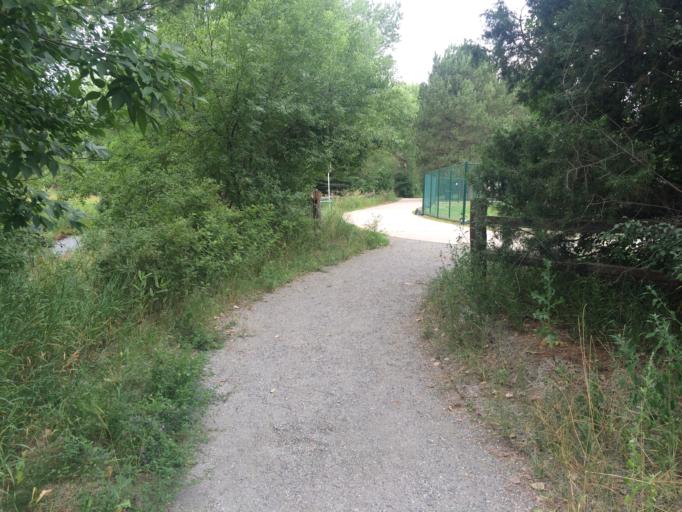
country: US
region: Colorado
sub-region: Jefferson County
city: Wheat Ridge
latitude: 39.7743
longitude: -105.0990
